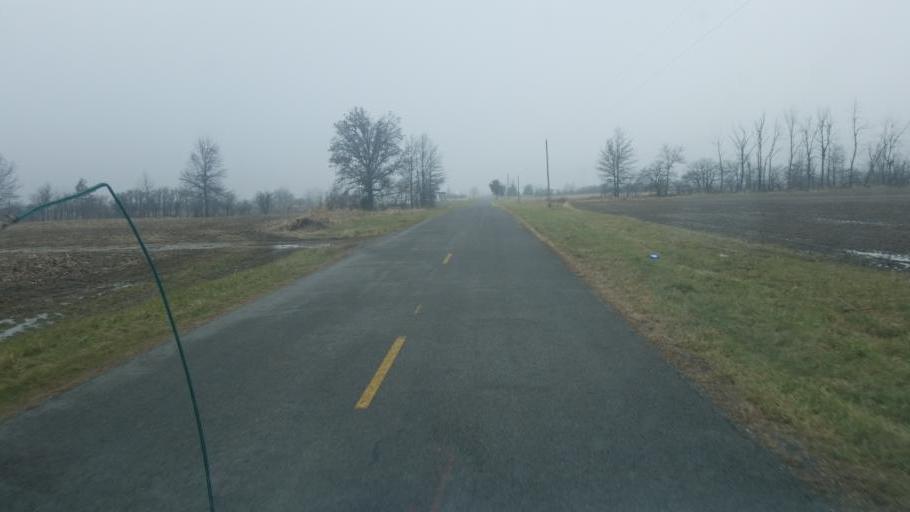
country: US
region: Ohio
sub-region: Logan County
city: Northwood
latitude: 40.4635
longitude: -83.5439
